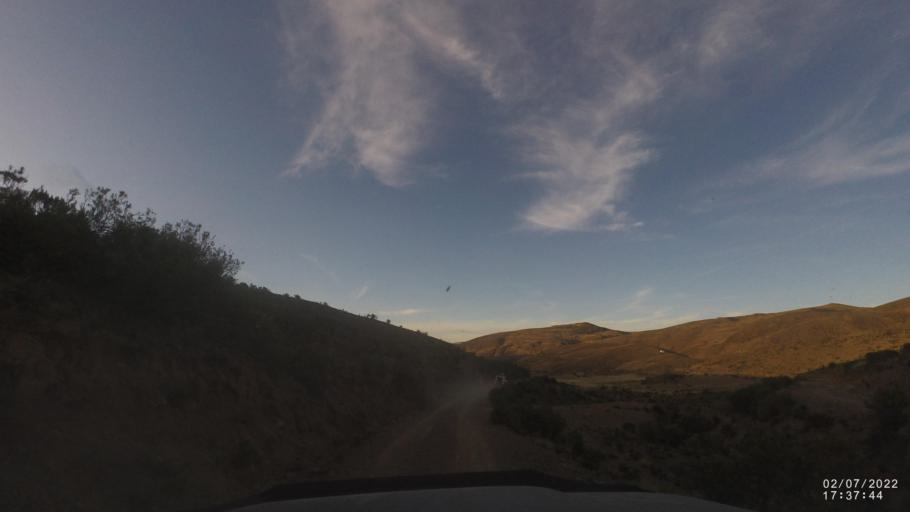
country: BO
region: Cochabamba
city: Irpa Irpa
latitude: -17.8718
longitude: -66.6191
